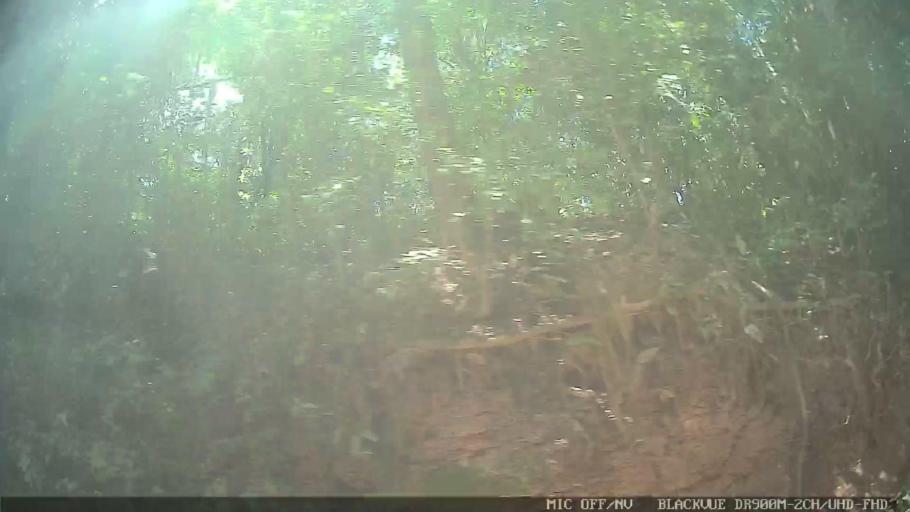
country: BR
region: Sao Paulo
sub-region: Conchas
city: Conchas
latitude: -23.0519
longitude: -47.9868
